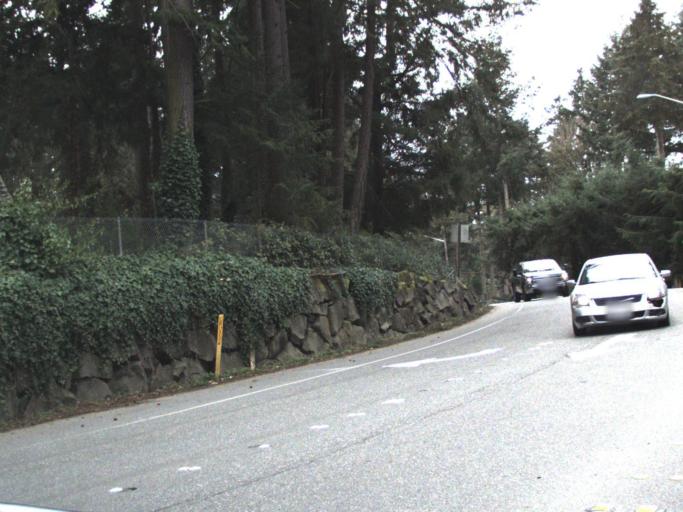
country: US
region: Washington
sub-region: King County
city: Federal Way
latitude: 47.3208
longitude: -122.3614
